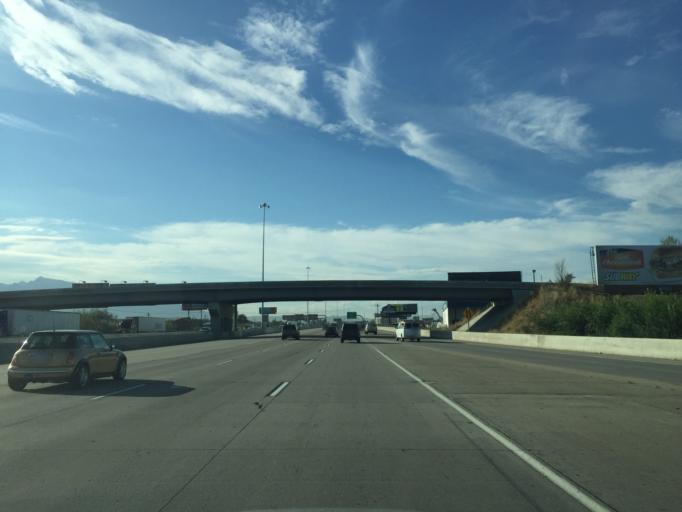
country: US
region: Utah
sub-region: Salt Lake County
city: South Salt Lake
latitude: 40.7136
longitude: -111.9045
